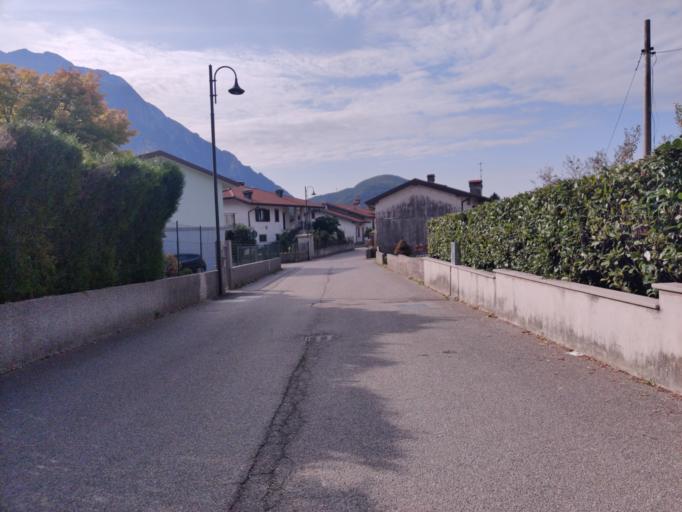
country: IT
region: Friuli Venezia Giulia
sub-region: Provincia di Udine
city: Venzone
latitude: 46.3312
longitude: 13.1397
